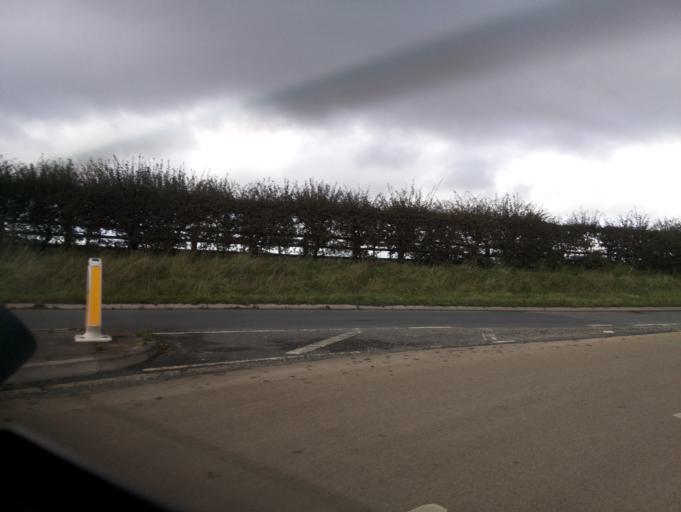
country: GB
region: England
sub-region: Devon
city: Kingsbridge
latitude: 50.2974
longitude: -3.7977
